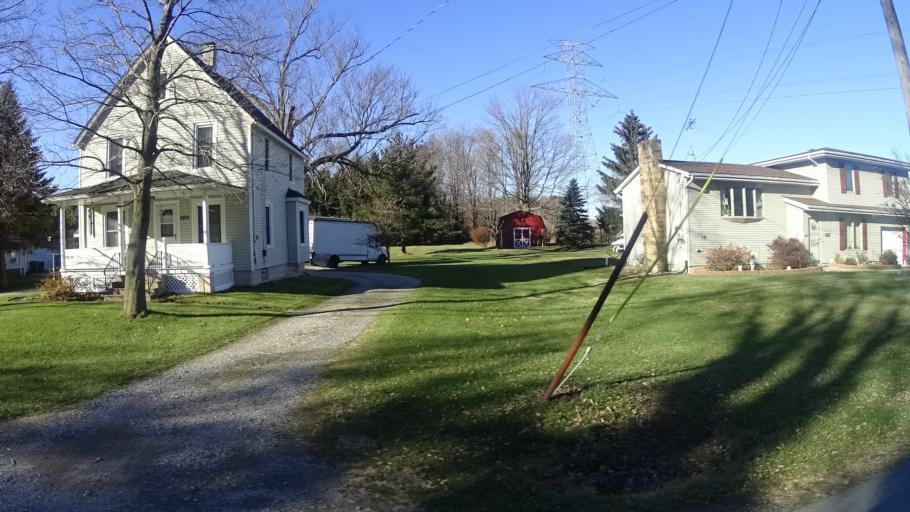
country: US
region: Ohio
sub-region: Lorain County
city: Sheffield
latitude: 41.4133
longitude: -82.1133
